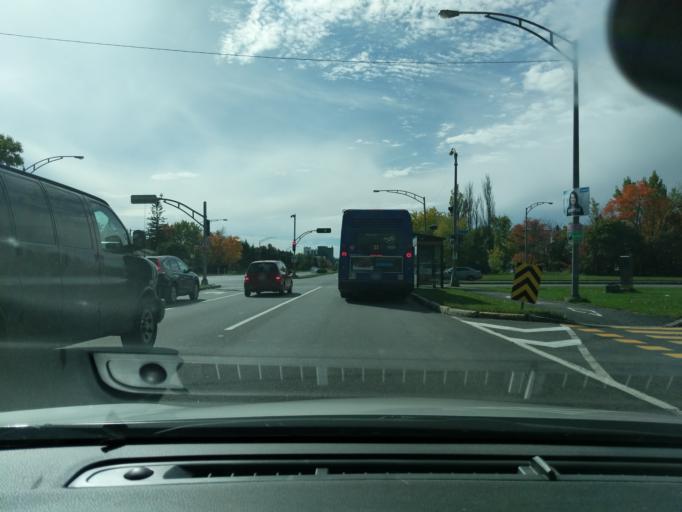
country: CA
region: Quebec
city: Quebec
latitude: 46.7798
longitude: -71.2643
